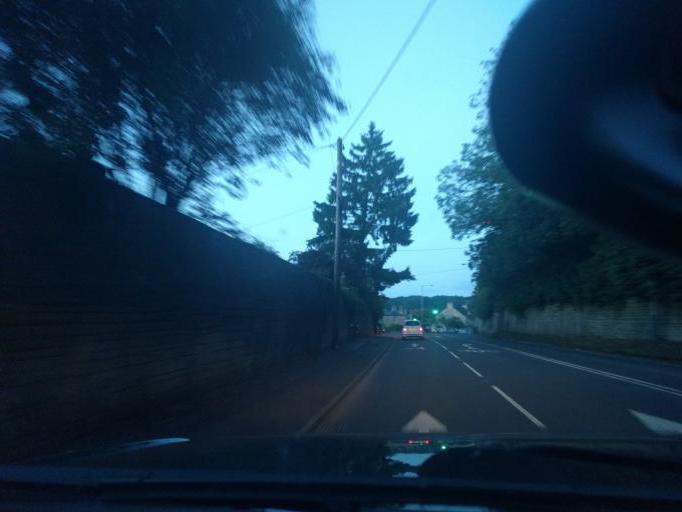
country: GB
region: England
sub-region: Wiltshire
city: Box
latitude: 51.4143
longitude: -2.2563
